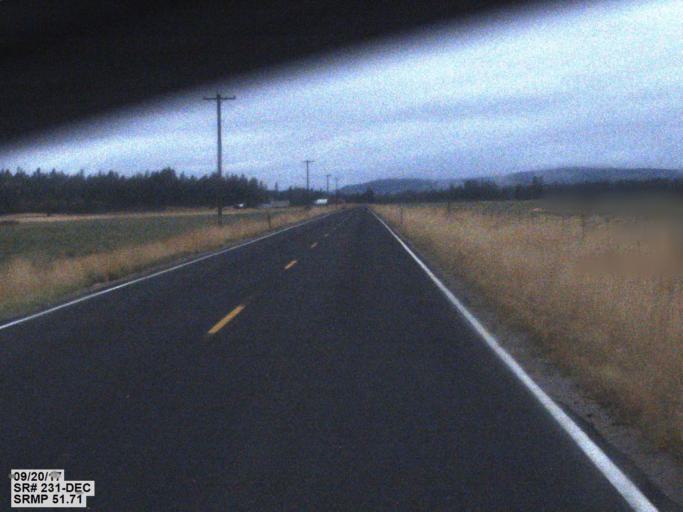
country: US
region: Washington
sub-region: Spokane County
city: Deer Park
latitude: 47.9213
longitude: -117.7864
